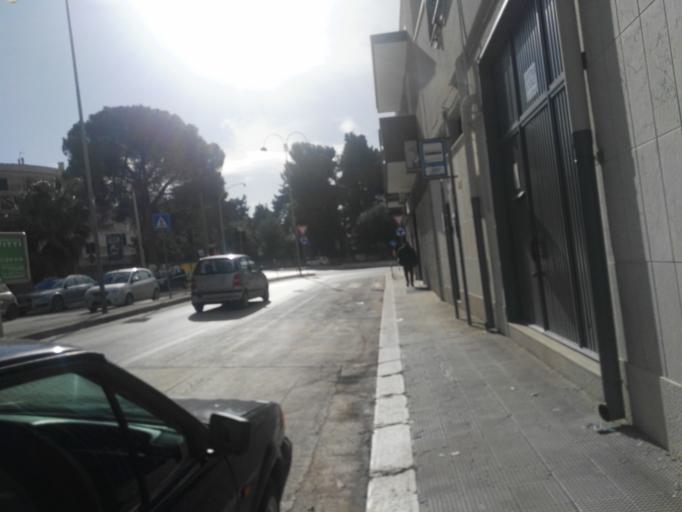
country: IT
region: Apulia
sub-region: Provincia di Barletta - Andria - Trani
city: Andria
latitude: 41.2197
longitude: 16.3061
